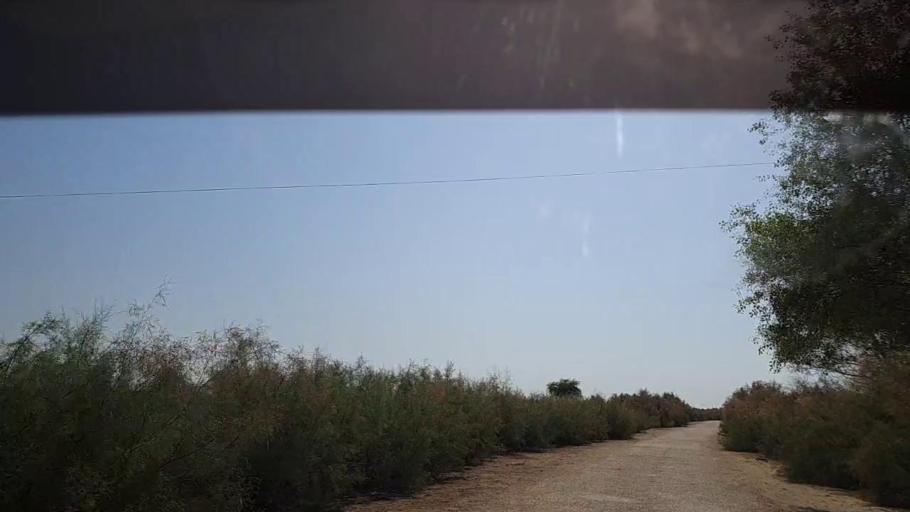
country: PK
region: Sindh
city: Ghauspur
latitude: 28.2042
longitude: 69.0765
